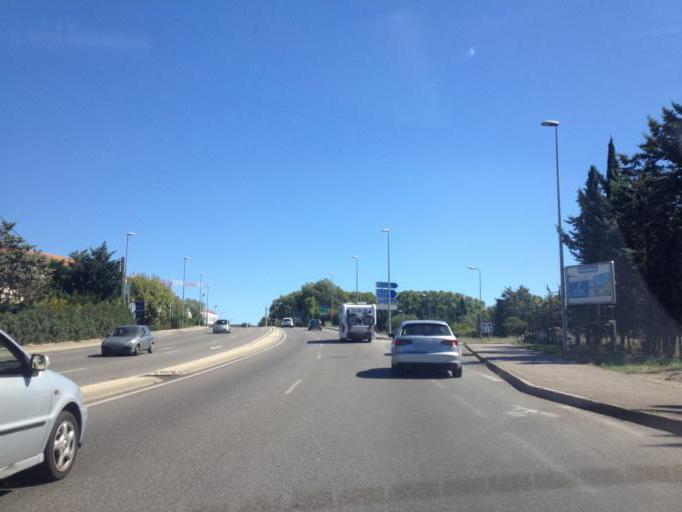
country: FR
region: Provence-Alpes-Cote d'Azur
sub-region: Departement des Bouches-du-Rhone
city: Aix-en-Provence
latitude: 43.5285
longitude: 5.4247
